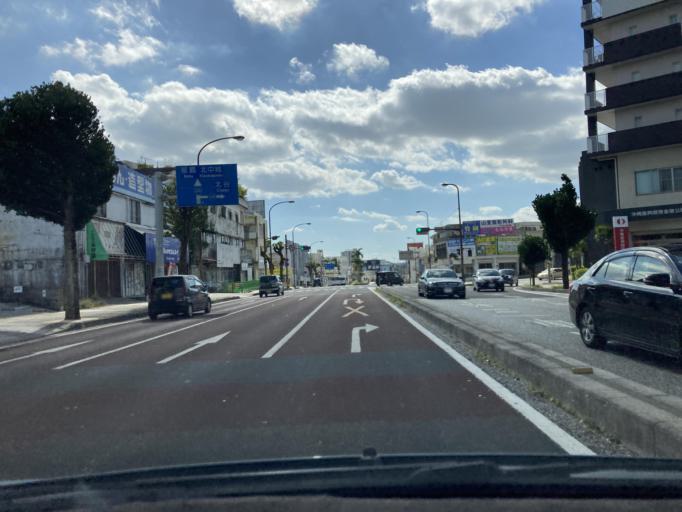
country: JP
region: Okinawa
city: Okinawa
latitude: 26.3241
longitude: 127.7931
